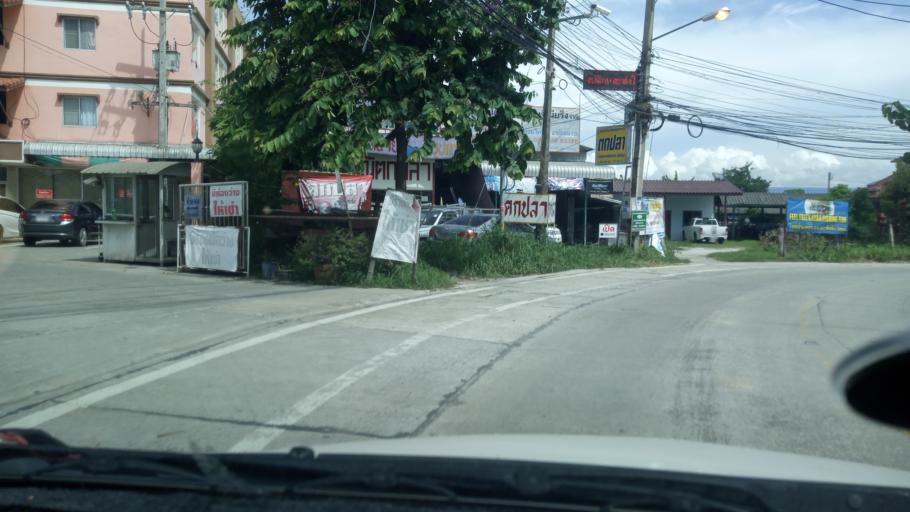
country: TH
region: Chon Buri
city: Chon Buri
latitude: 13.4163
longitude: 101.0289
